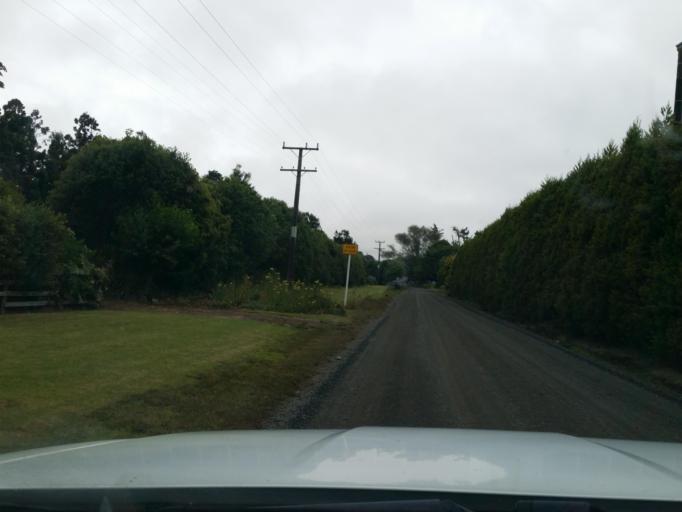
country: NZ
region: Northland
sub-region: Kaipara District
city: Dargaville
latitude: -36.0381
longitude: 173.9202
